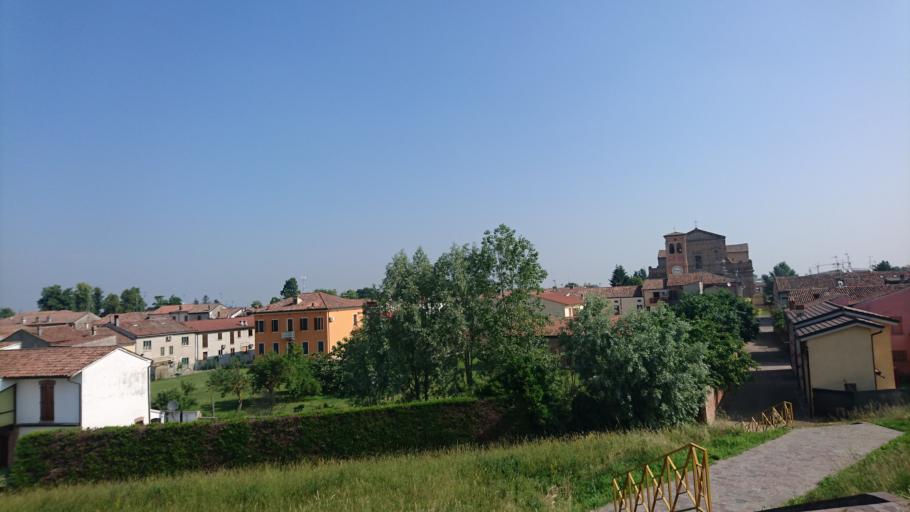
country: IT
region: Veneto
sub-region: Provincia di Rovigo
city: Melara
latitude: 45.0610
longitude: 11.2004
